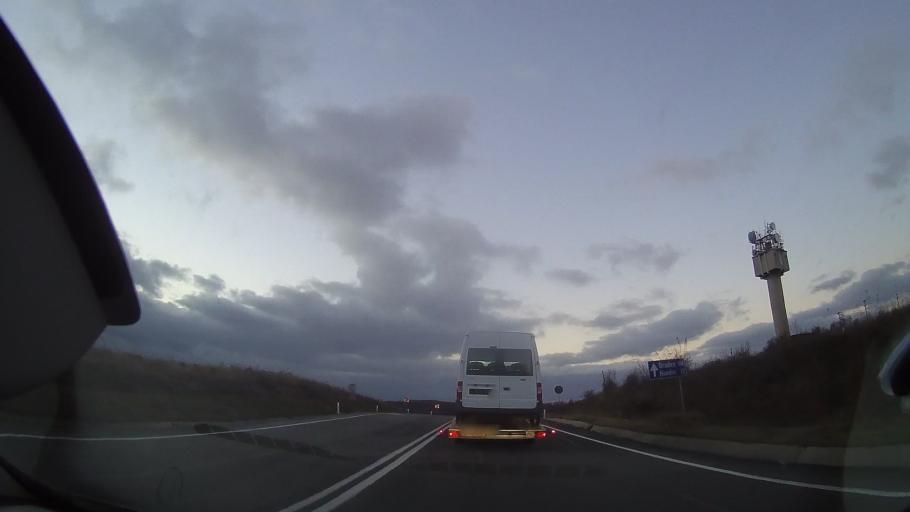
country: RO
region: Cluj
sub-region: Comuna Izvoru Crisului
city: Izvoru Crisului
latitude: 46.8259
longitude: 23.1550
